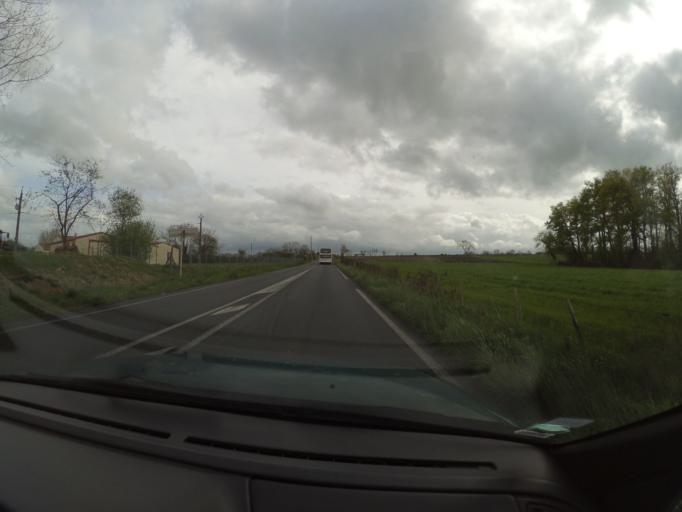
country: FR
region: Pays de la Loire
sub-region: Departement de Maine-et-Loire
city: Lire
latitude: 47.3191
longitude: -1.1642
